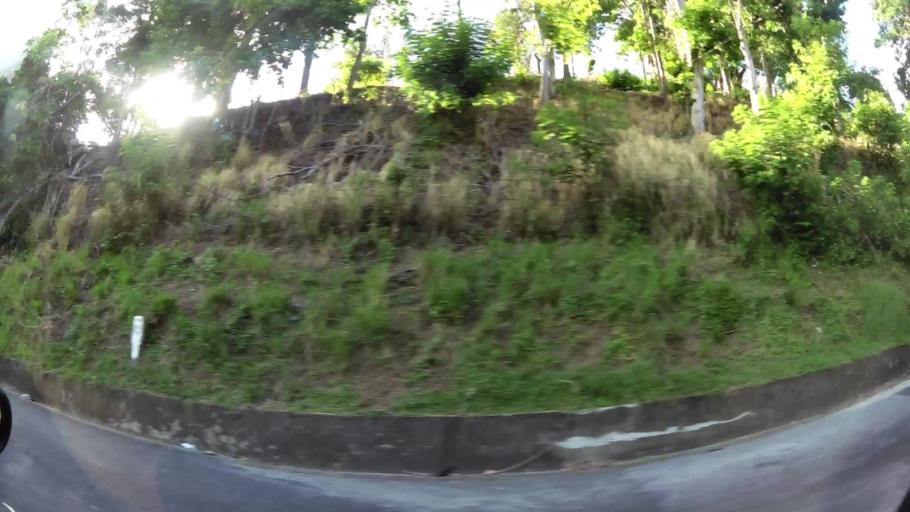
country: TT
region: Eastern Tobago
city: Roxborough
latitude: 11.2293
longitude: -60.6091
